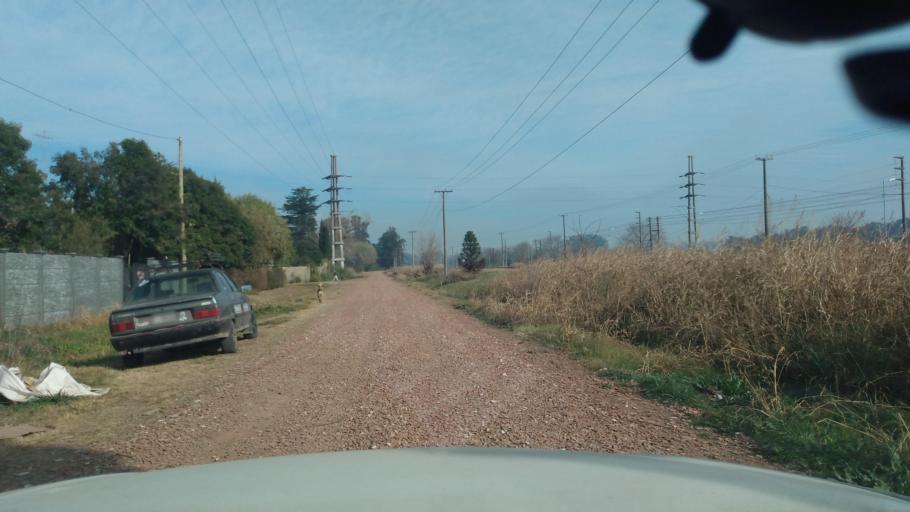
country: AR
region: Buenos Aires
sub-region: Partido de Lujan
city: Lujan
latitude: -34.5889
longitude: -59.1378
